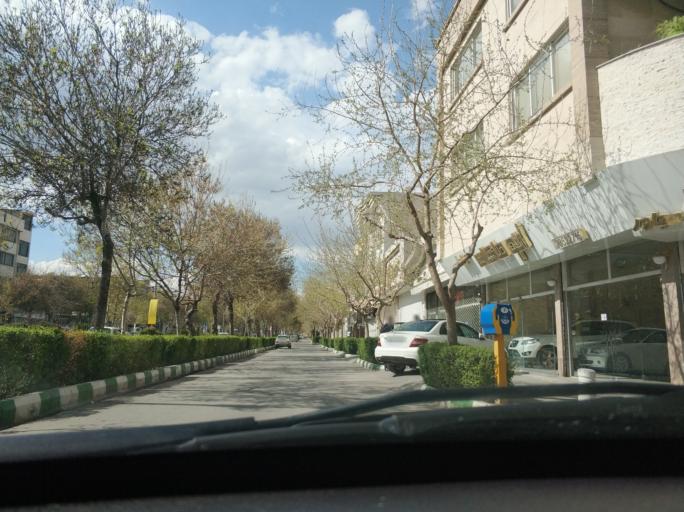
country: IR
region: Razavi Khorasan
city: Mashhad
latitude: 36.2708
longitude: 59.5962
